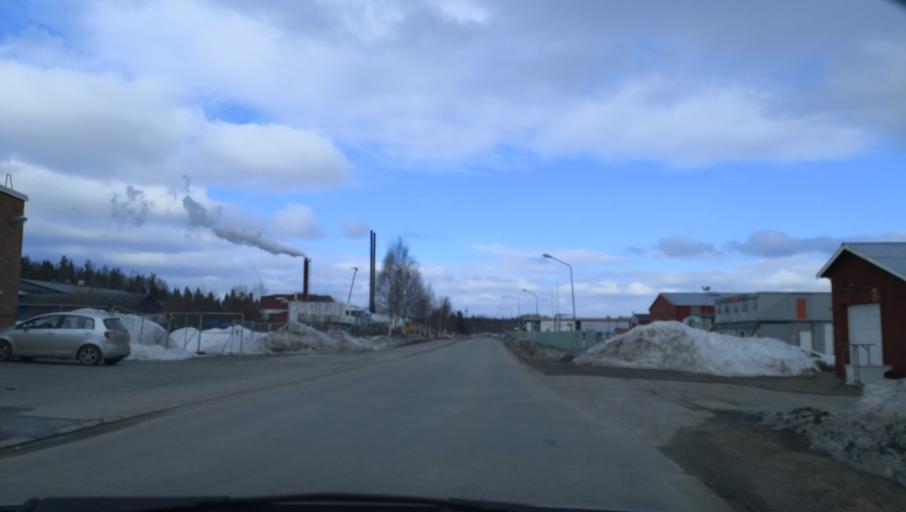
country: SE
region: Vaesterbotten
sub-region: Vannas Kommun
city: Vaennaes
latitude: 63.9137
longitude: 19.7441
